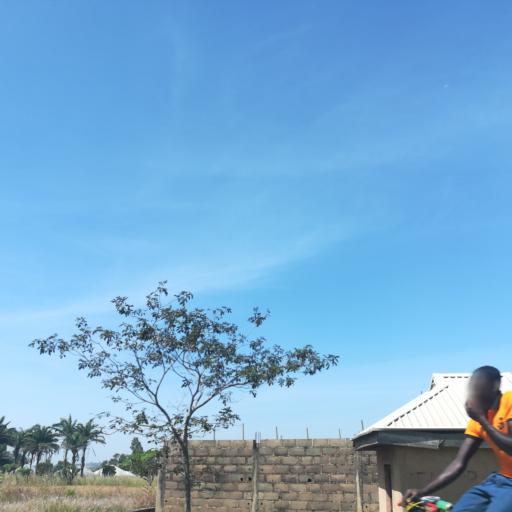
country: NG
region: Plateau
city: Bukuru
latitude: 9.7799
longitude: 8.8860
